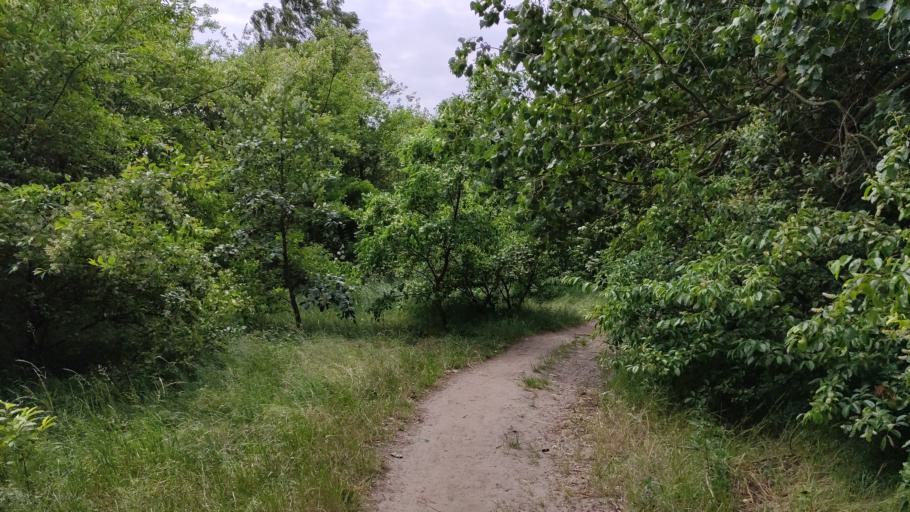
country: DE
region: Mecklenburg-Vorpommern
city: Bastorf
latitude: 54.1320
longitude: 11.6502
